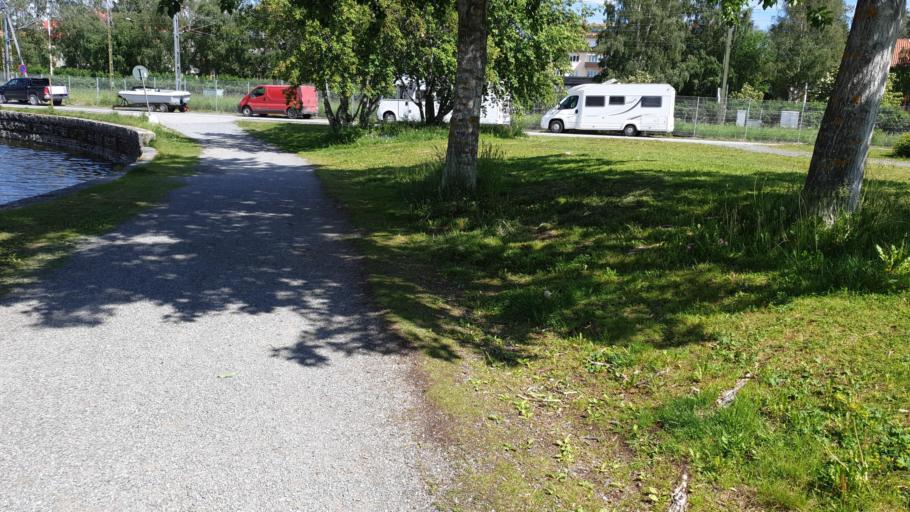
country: SE
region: Jaemtland
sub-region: OEstersunds Kommun
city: Ostersund
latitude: 63.1754
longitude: 14.6306
